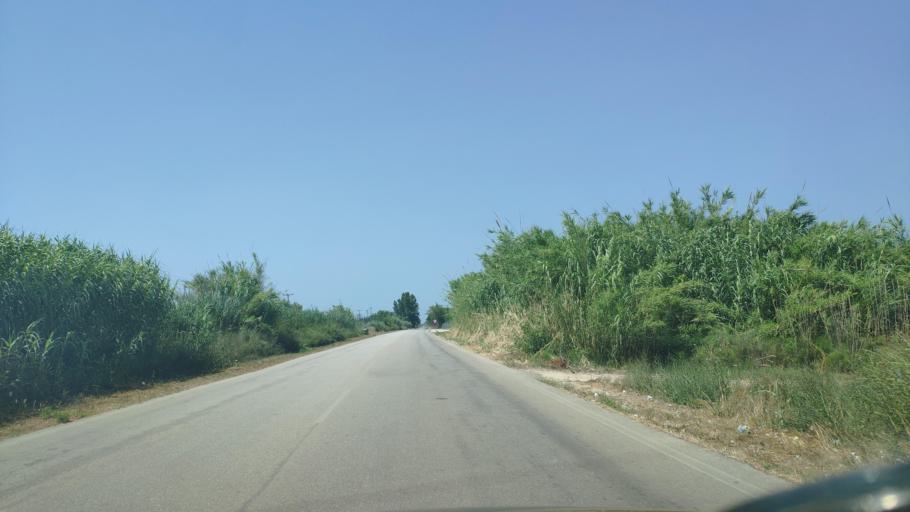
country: GR
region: Epirus
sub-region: Nomos Artas
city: Aneza
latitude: 39.1153
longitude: 20.9290
